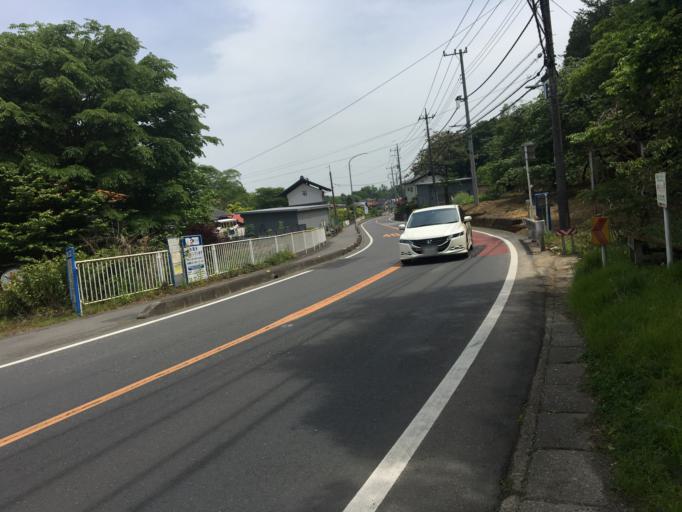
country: JP
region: Saitama
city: Hanno
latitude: 35.8541
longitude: 139.3031
